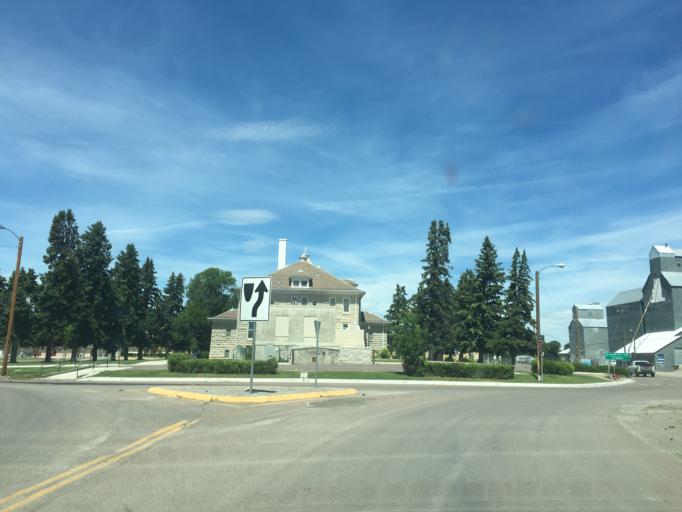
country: US
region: Montana
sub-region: Teton County
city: Choteau
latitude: 47.8099
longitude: -112.1815
